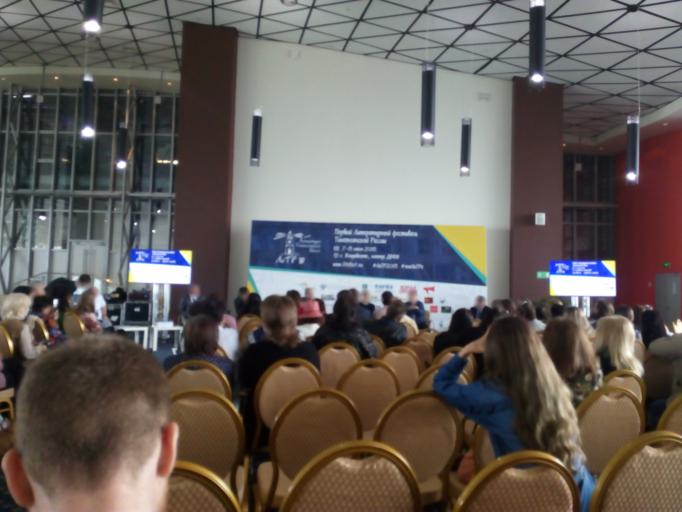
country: RU
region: Primorskiy
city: Russkiy
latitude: 43.0246
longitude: 131.8937
